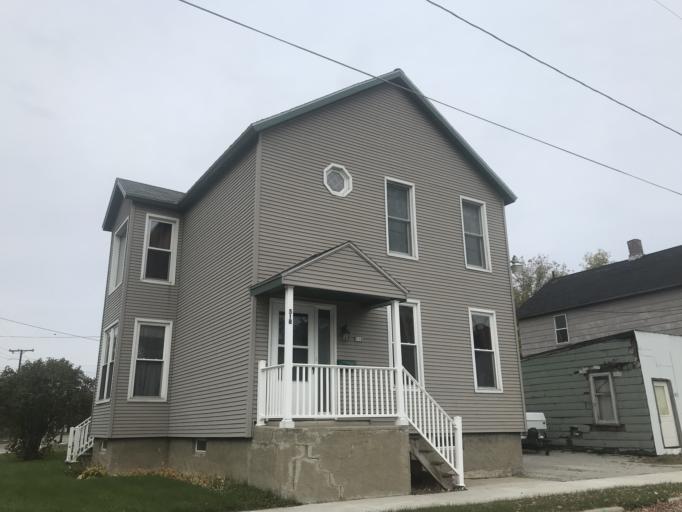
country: US
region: Michigan
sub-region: Menominee County
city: Menominee
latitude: 45.1101
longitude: -87.6094
